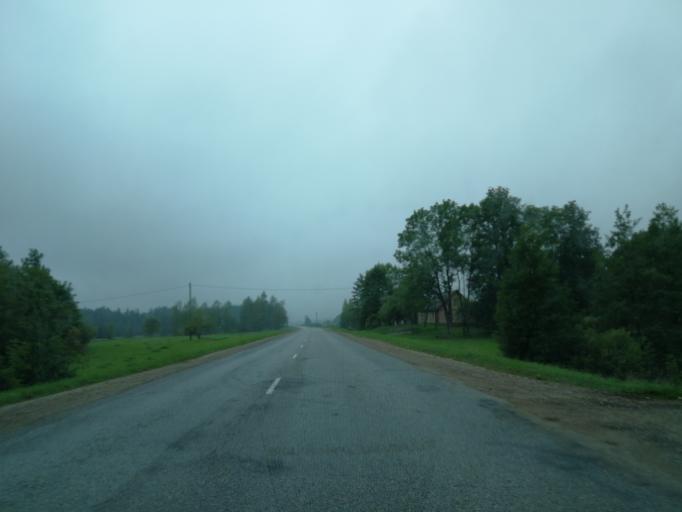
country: LV
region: Varkava
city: Vecvarkava
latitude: 56.3129
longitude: 26.5349
